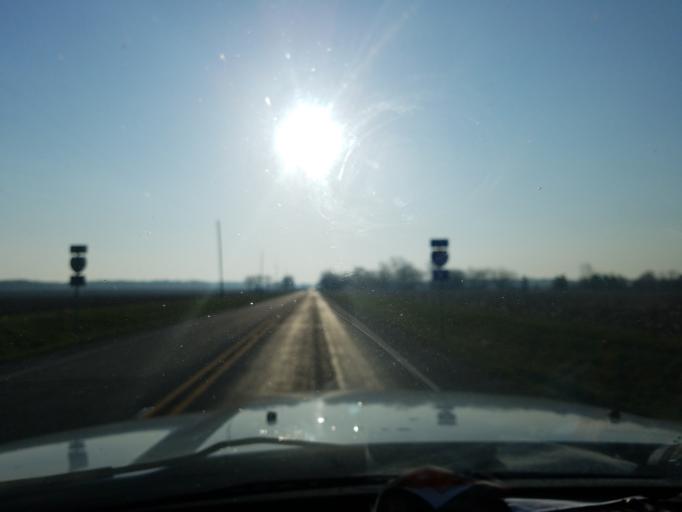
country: US
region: Indiana
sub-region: Vigo County
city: Seelyville
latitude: 39.3892
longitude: -87.2057
